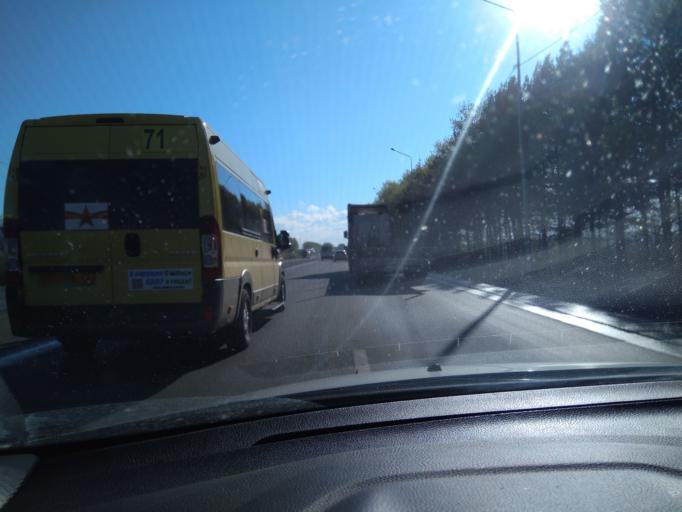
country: RU
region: Tjumen
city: Moskovskiy
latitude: 57.1221
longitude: 65.4526
